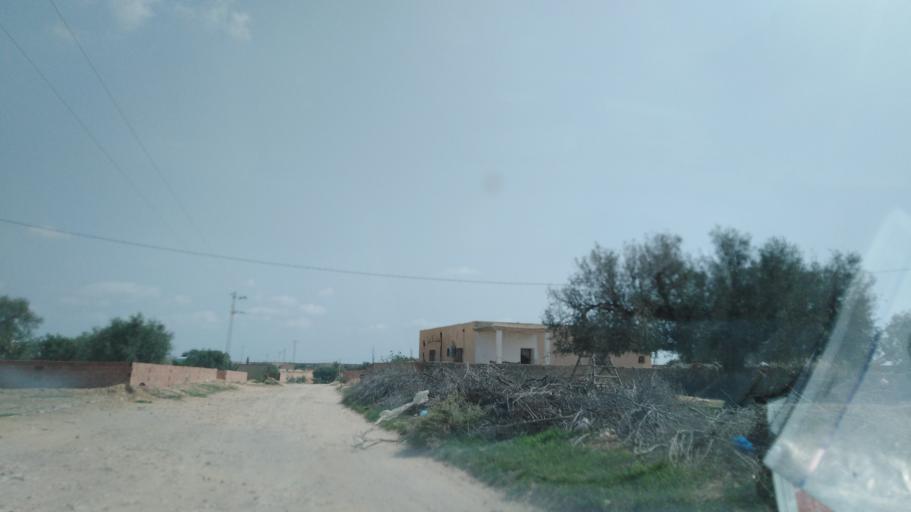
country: TN
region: Safaqis
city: Sfax
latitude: 34.6386
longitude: 10.6139
